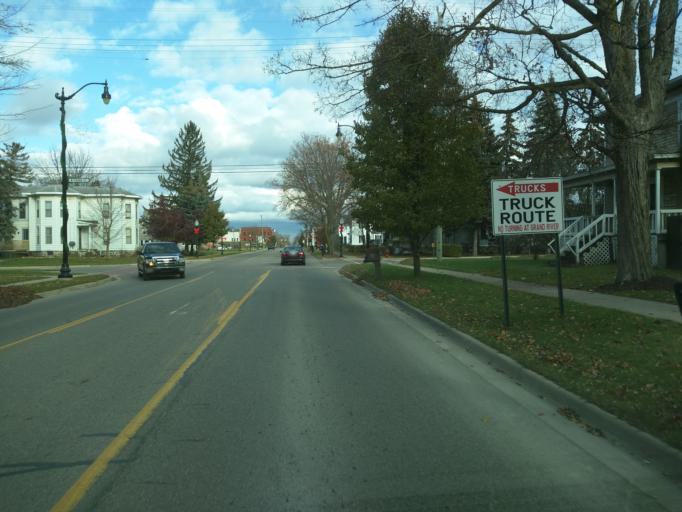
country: US
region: Michigan
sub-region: Livingston County
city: Fowlerville
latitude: 42.6577
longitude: -84.0730
